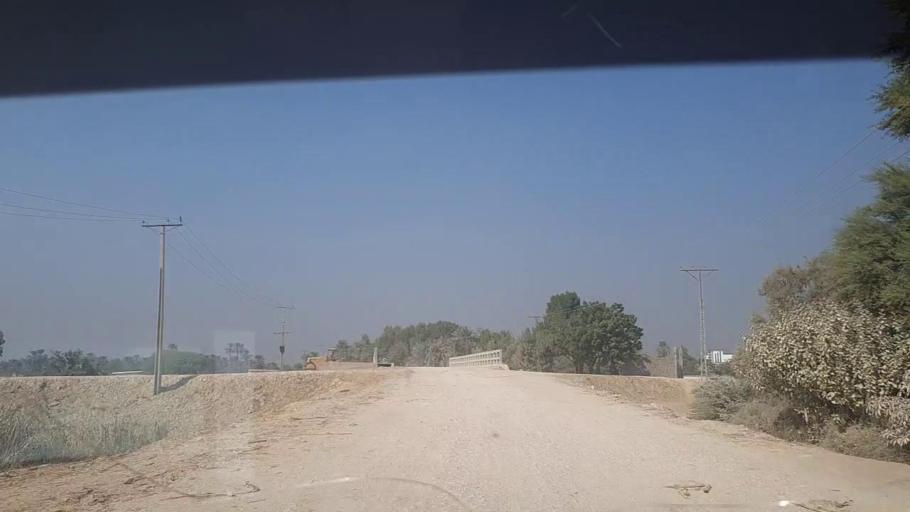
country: PK
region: Sindh
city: Kot Diji
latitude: 27.3584
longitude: 68.7101
